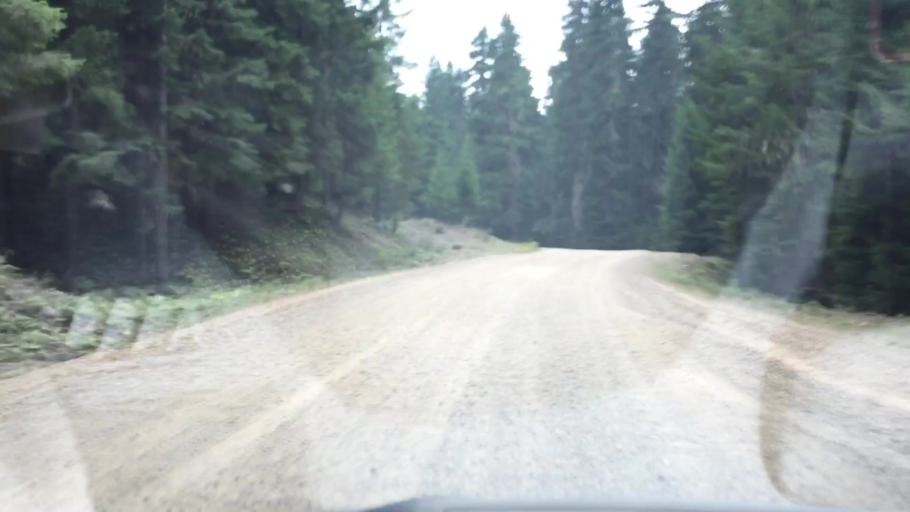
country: US
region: Washington
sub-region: Klickitat County
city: White Salmon
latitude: 46.2359
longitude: -121.6292
